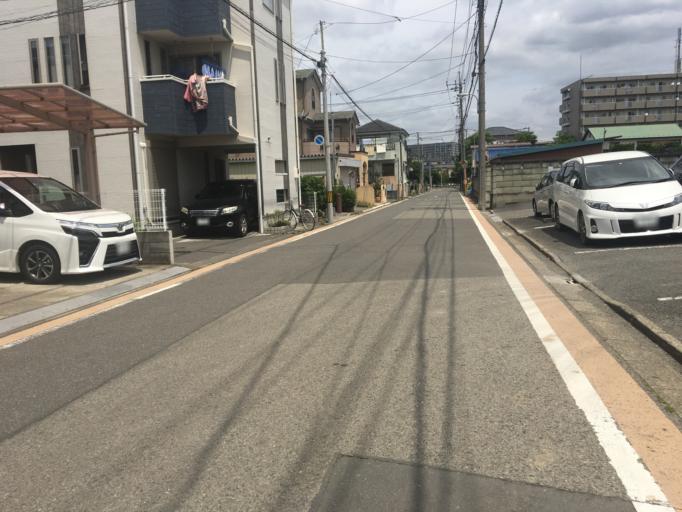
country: JP
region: Saitama
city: Shimotoda
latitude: 35.8021
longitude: 139.6857
